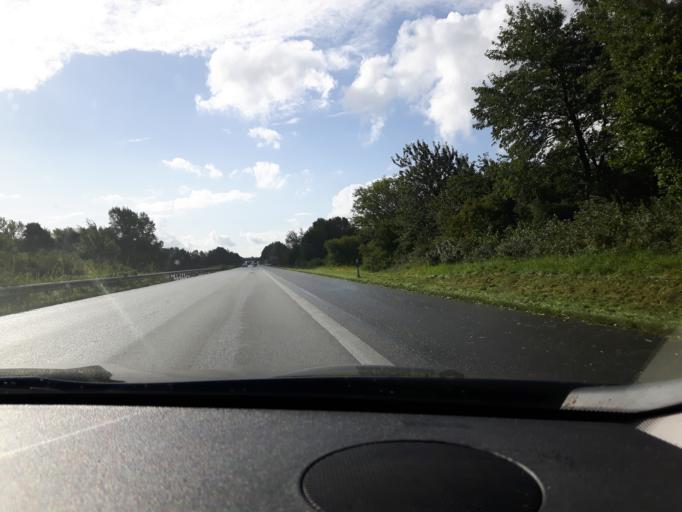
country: DE
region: Schleswig-Holstein
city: Handewitt
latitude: 54.7949
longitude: 9.3337
